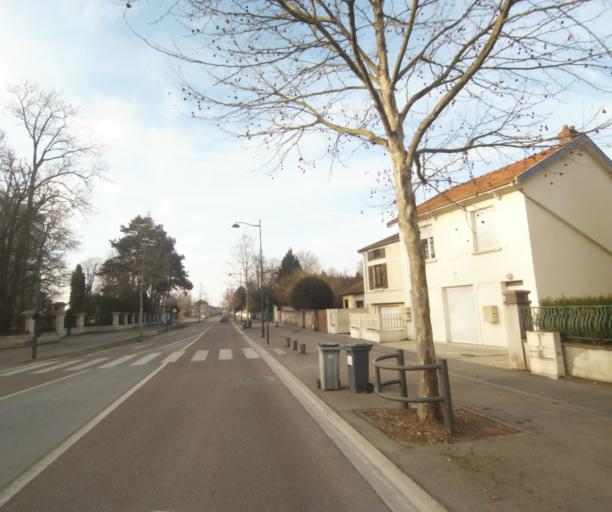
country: FR
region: Champagne-Ardenne
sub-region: Departement de la Haute-Marne
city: Saint-Dizier
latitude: 48.6446
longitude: 4.9531
